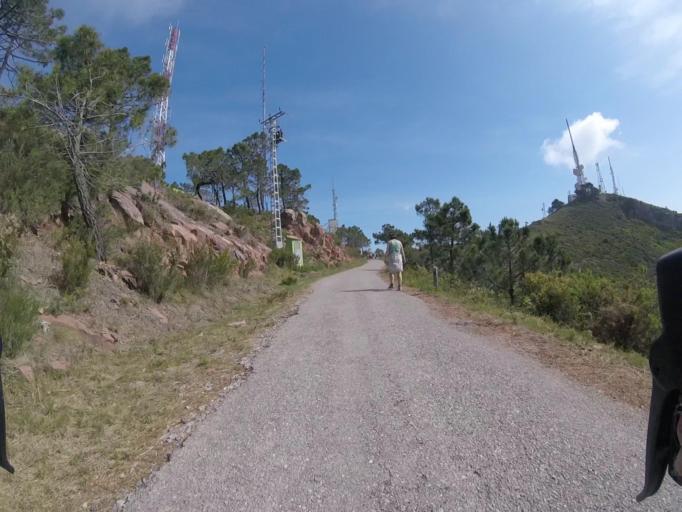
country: ES
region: Valencia
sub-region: Provincia de Castello
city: Benicassim
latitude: 40.0849
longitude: 0.0280
